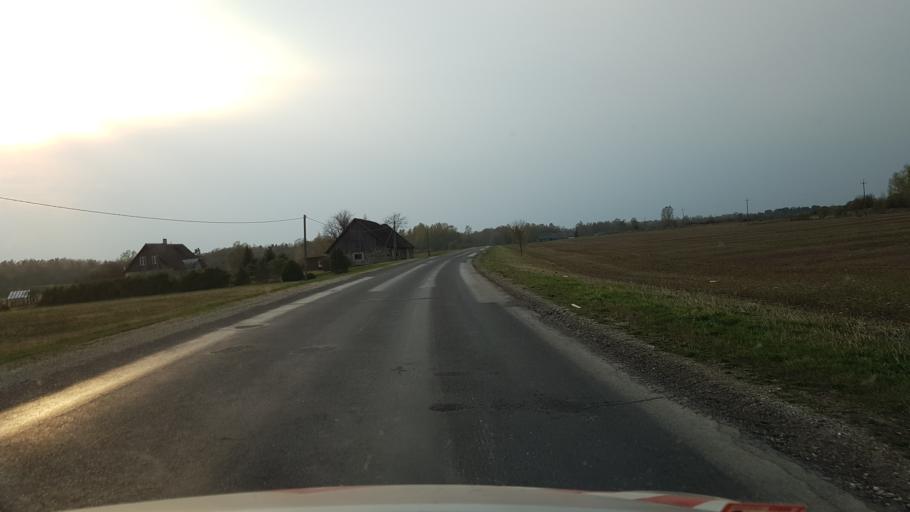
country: EE
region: Harju
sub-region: Raasiku vald
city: Raasiku
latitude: 59.3396
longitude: 25.1416
